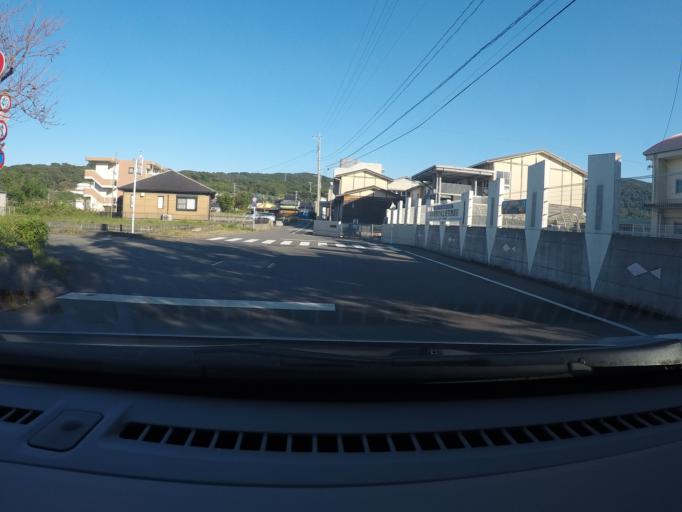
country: JP
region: Kumamoto
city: Minamata
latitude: 32.1763
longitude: 130.3796
